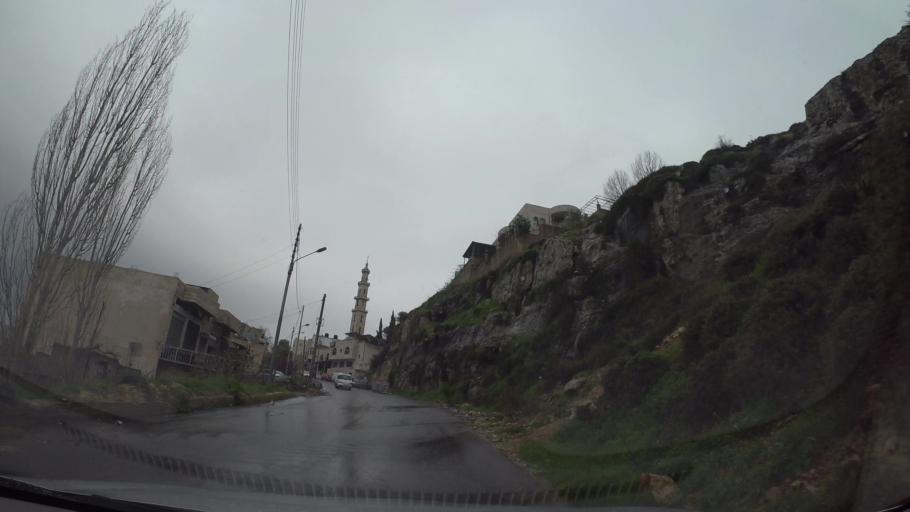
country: JO
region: Amman
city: Al Jubayhah
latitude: 32.0320
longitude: 35.8319
